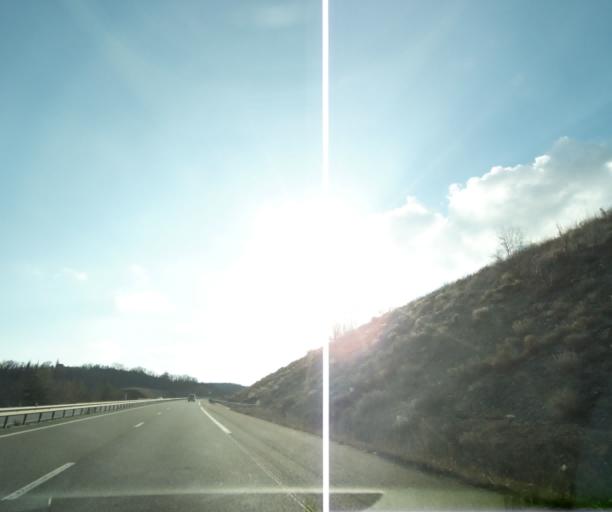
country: FR
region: Midi-Pyrenees
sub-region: Departement du Lot
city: Lalbenque
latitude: 44.3869
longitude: 1.5152
